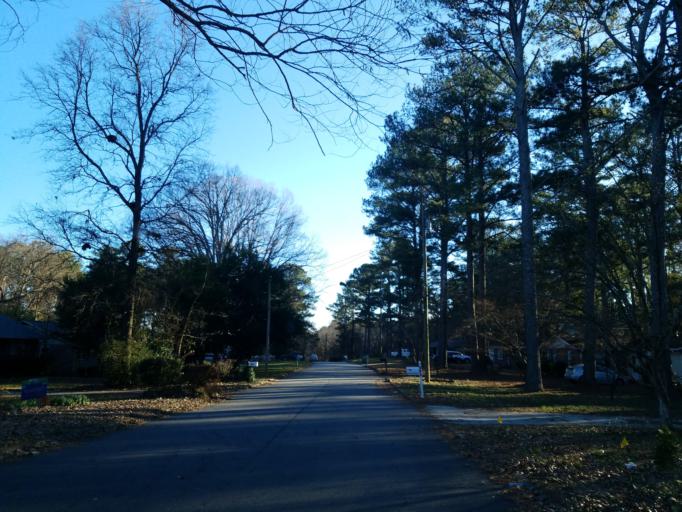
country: US
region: Georgia
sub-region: Cobb County
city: Fair Oaks
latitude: 33.9382
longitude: -84.4932
